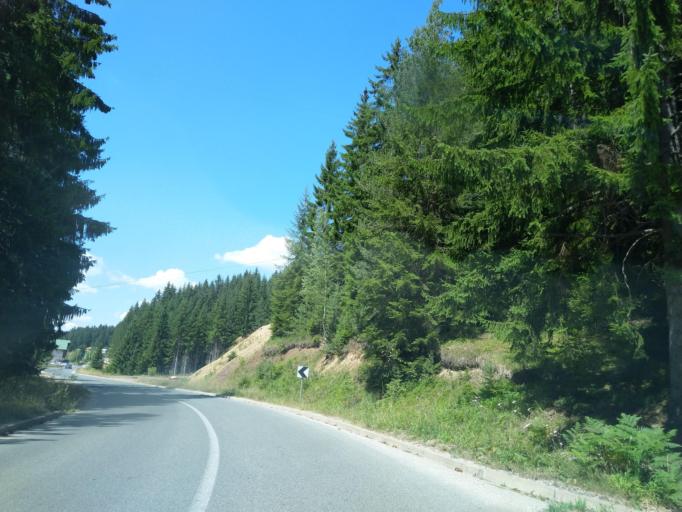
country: RS
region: Central Serbia
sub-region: Zlatiborski Okrug
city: Nova Varos
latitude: 43.4369
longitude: 19.8237
